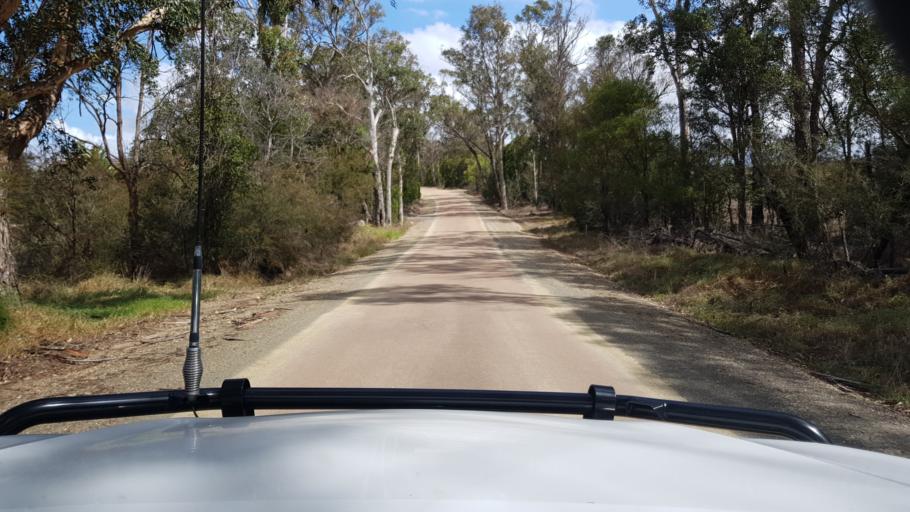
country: AU
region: Victoria
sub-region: East Gippsland
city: Bairnsdale
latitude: -37.7684
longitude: 147.6075
